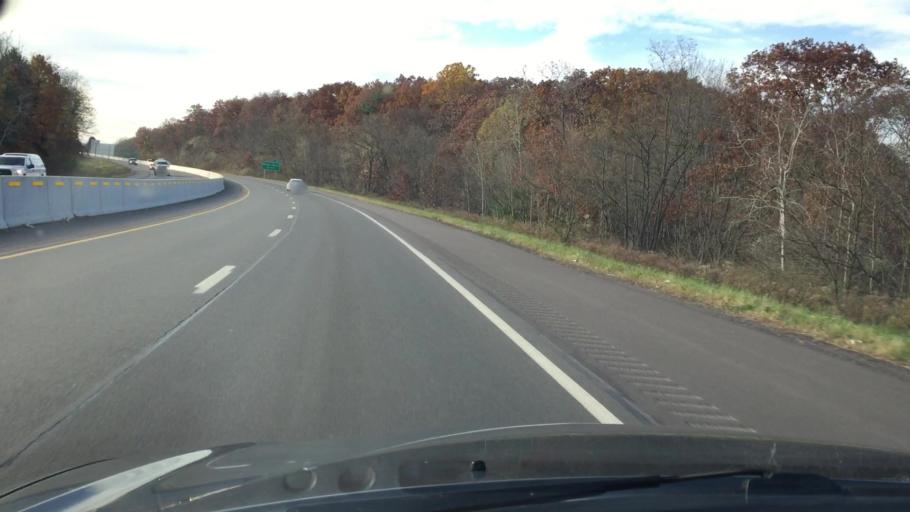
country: US
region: Pennsylvania
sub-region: Luzerne County
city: Ashley
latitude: 41.2029
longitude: -75.9322
